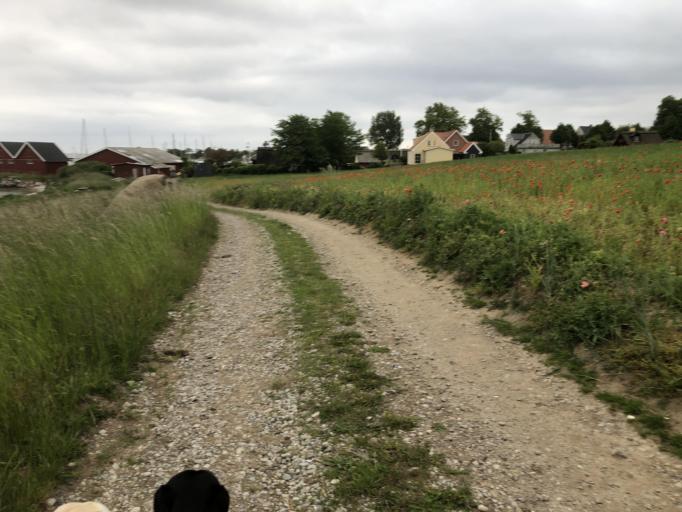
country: DK
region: Zealand
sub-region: Slagelse Kommune
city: Skaelskor
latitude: 55.2128
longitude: 11.1968
